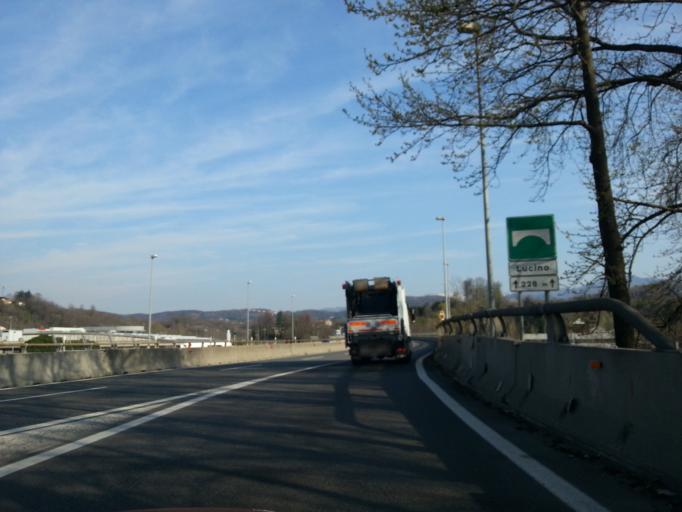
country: IT
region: Lombardy
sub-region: Provincia di Como
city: Lucino
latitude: 45.7836
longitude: 9.0517
